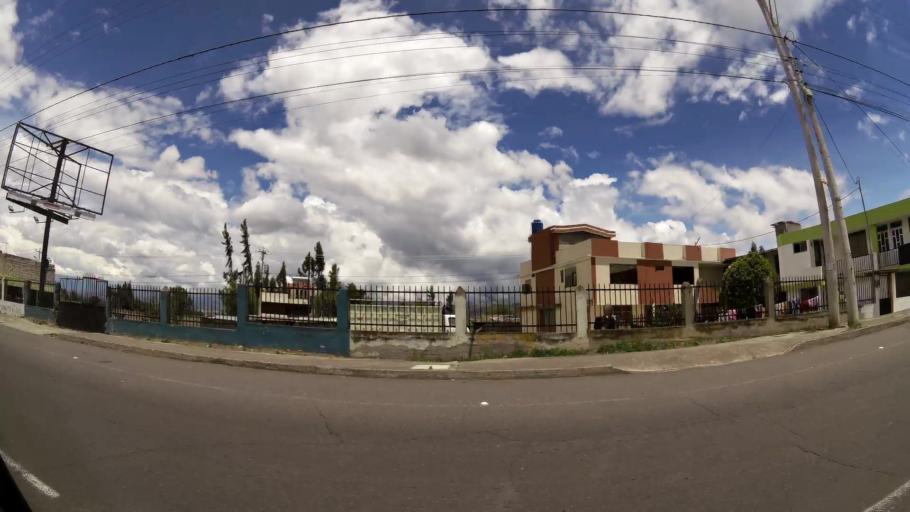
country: EC
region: Tungurahua
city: Ambato
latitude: -1.2929
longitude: -78.6040
